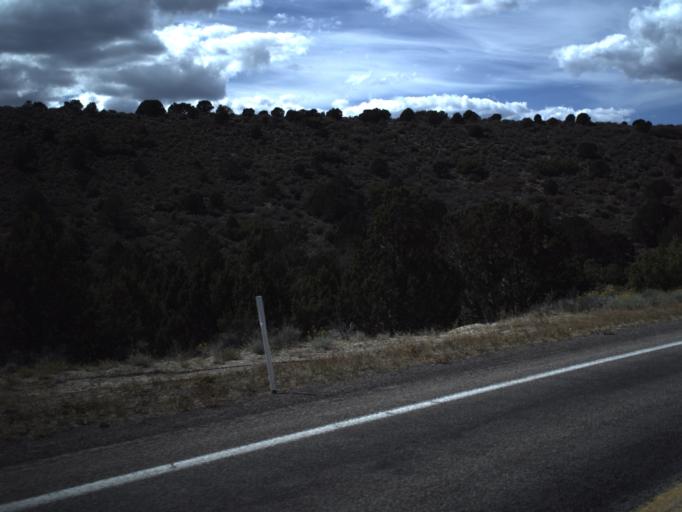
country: US
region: Utah
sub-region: Washington County
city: Enterprise
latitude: 37.5414
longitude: -113.6812
